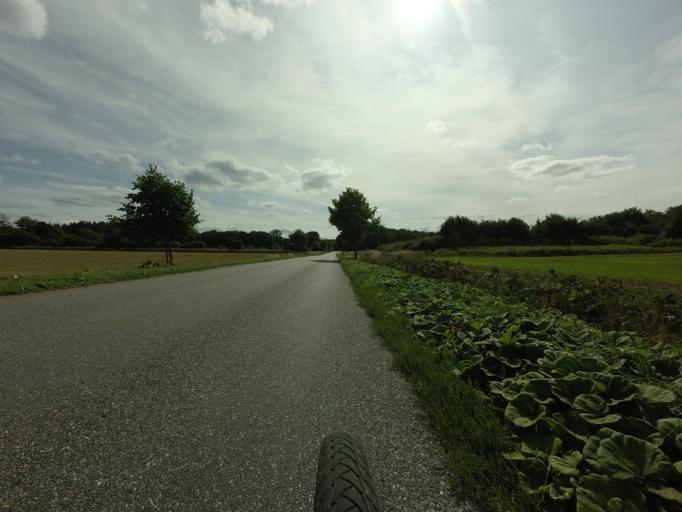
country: DK
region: Zealand
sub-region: Faxe Kommune
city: Fakse Ladeplads
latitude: 55.2407
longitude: 12.2165
